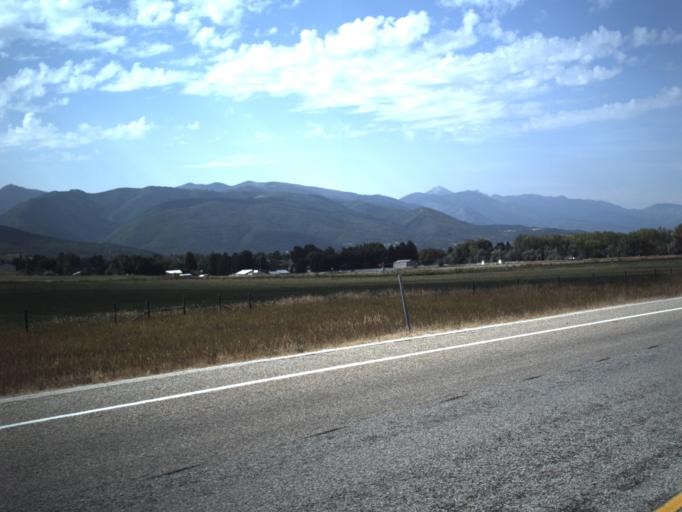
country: US
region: Utah
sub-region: Weber County
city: Wolf Creek
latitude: 41.2454
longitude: -111.7769
